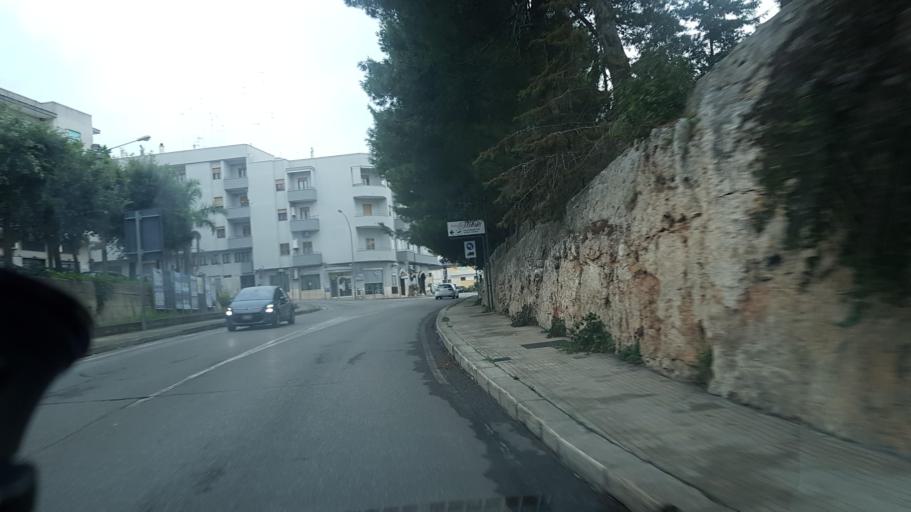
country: IT
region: Apulia
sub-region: Provincia di Brindisi
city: Ostuni
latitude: 40.7255
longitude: 17.5854
